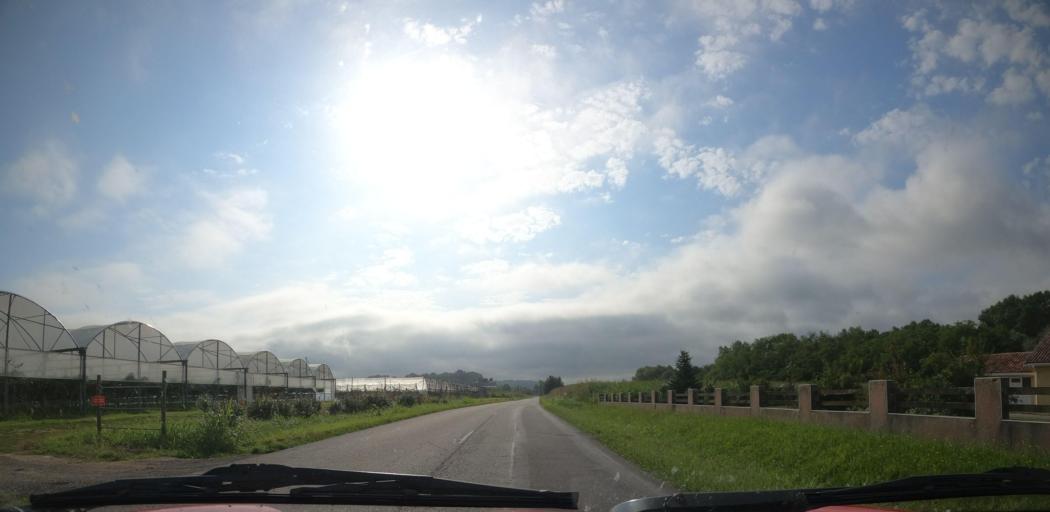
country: FR
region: Aquitaine
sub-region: Departement des Landes
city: Peyrehorade
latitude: 43.5369
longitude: -1.0755
